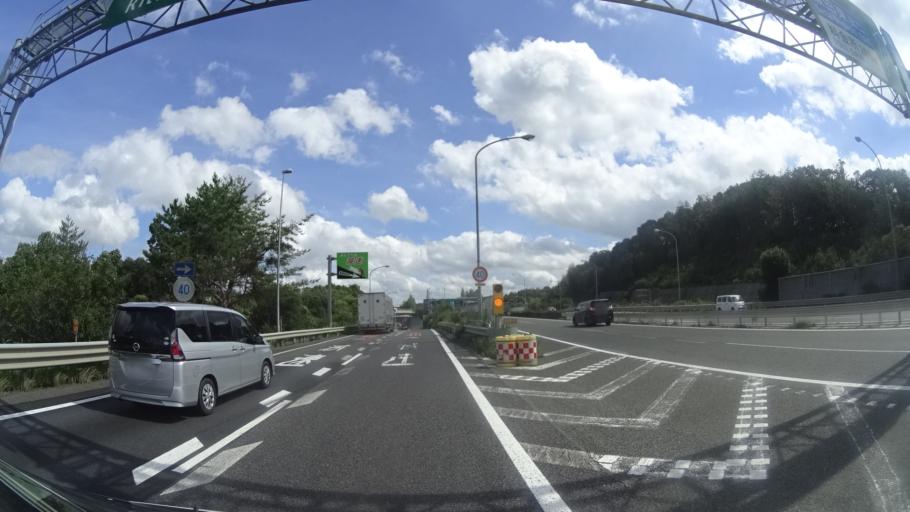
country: JP
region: Shiga Prefecture
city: Kusatsu
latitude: 34.9659
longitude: 135.9237
